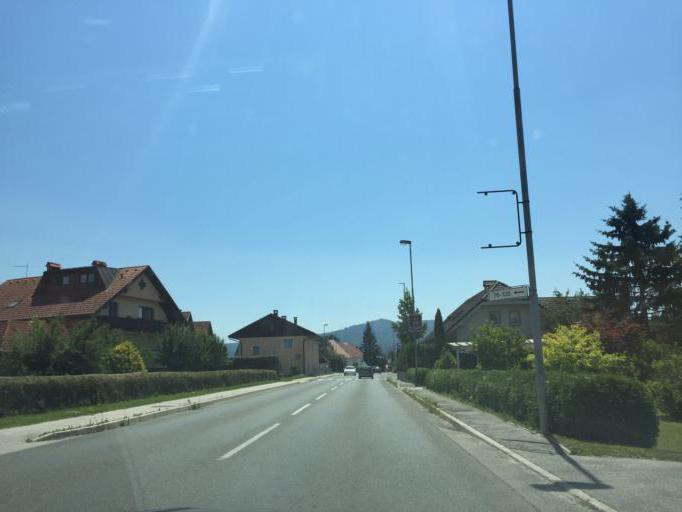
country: SI
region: Skofja Loka
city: Sv. Duh
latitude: 46.1833
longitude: 14.3232
